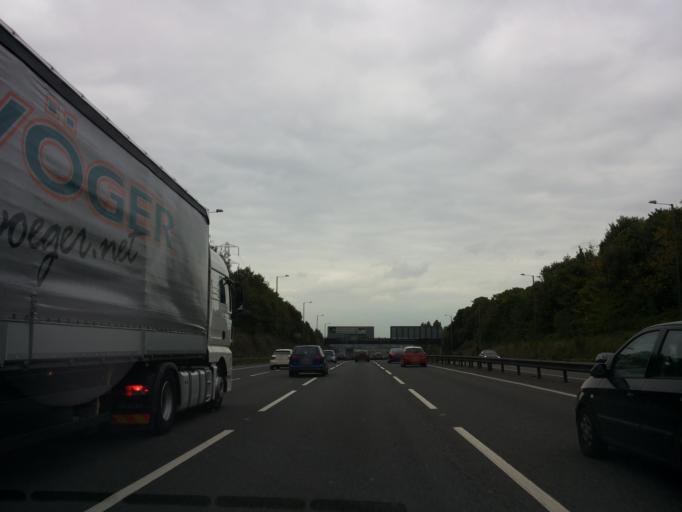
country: GB
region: England
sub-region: Kent
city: Swanscombe
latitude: 51.4306
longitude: 0.2997
